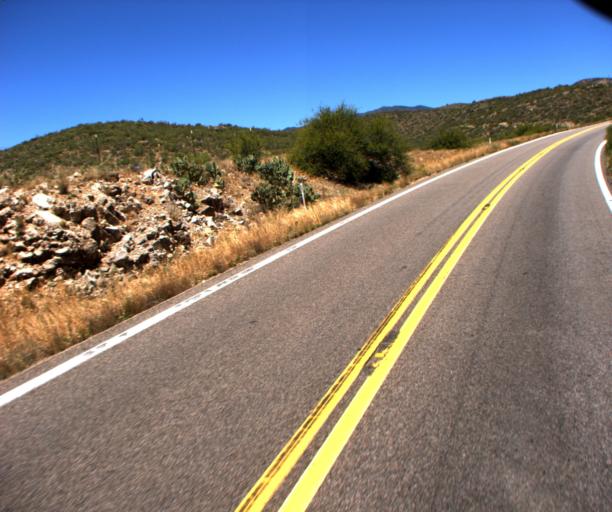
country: US
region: Arizona
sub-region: Pinal County
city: Kearny
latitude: 33.1822
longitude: -110.8116
